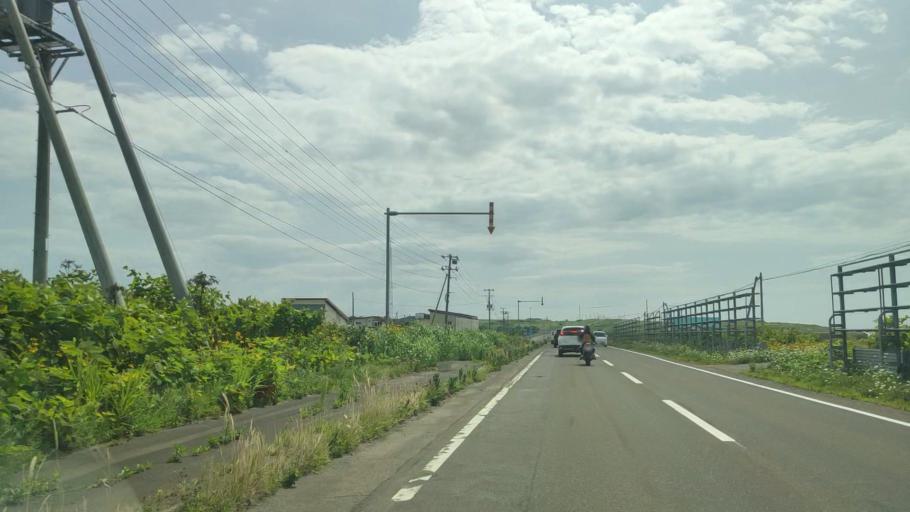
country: JP
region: Hokkaido
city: Rumoi
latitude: 44.4512
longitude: 141.7580
